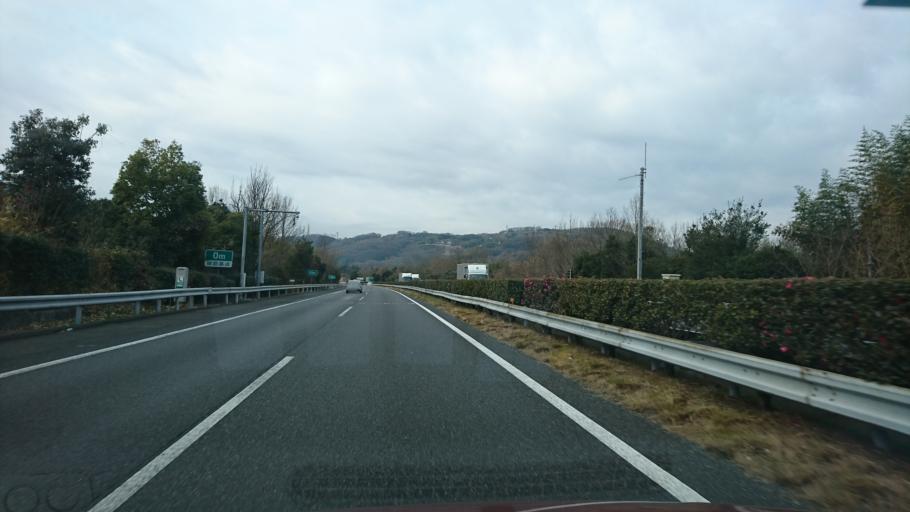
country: JP
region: Okayama
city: Kurashiki
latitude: 34.6046
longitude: 133.7172
